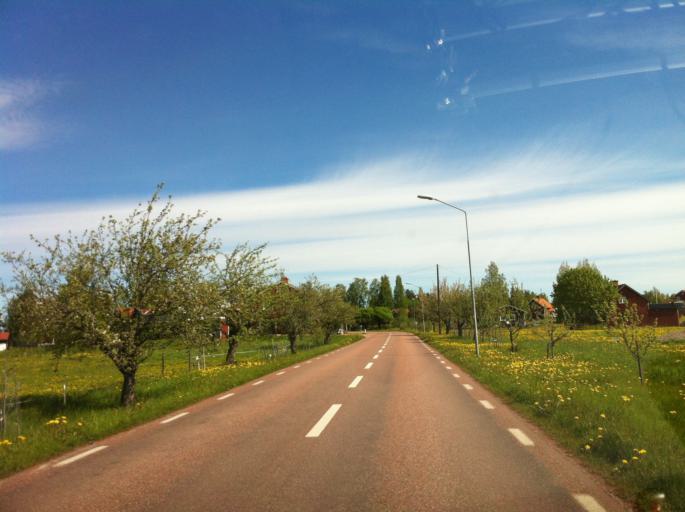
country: SE
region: Dalarna
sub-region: Mora Kommun
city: Mora
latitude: 60.9101
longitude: 14.6151
